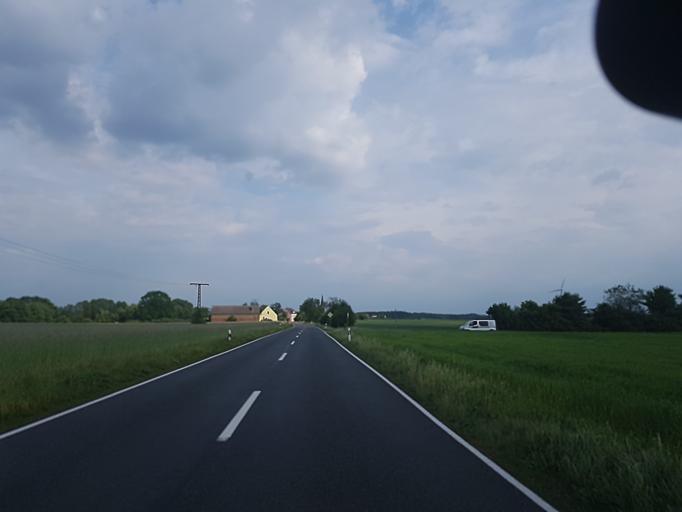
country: DE
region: Saxony-Anhalt
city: Klieken
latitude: 51.9160
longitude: 12.4048
